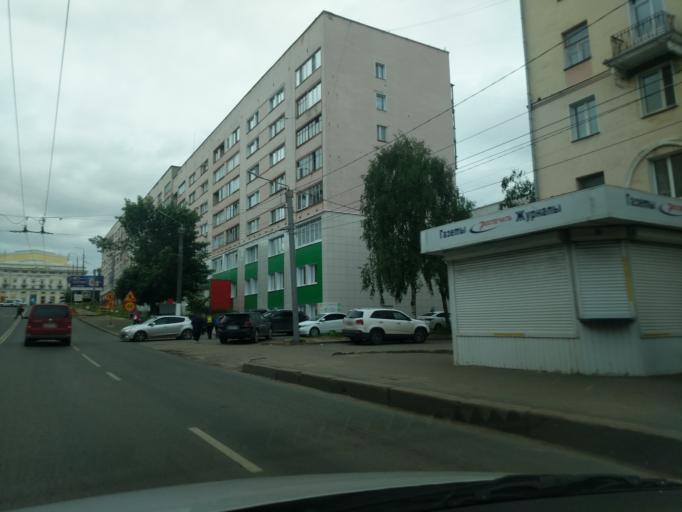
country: RU
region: Kirov
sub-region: Kirovo-Chepetskiy Rayon
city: Kirov
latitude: 58.6076
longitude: 49.6676
